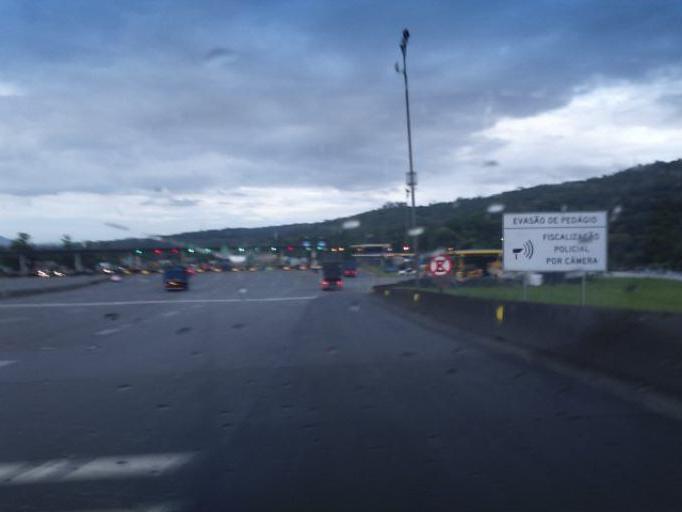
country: BR
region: Santa Catarina
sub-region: Joinville
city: Joinville
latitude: -25.9905
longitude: -48.8827
